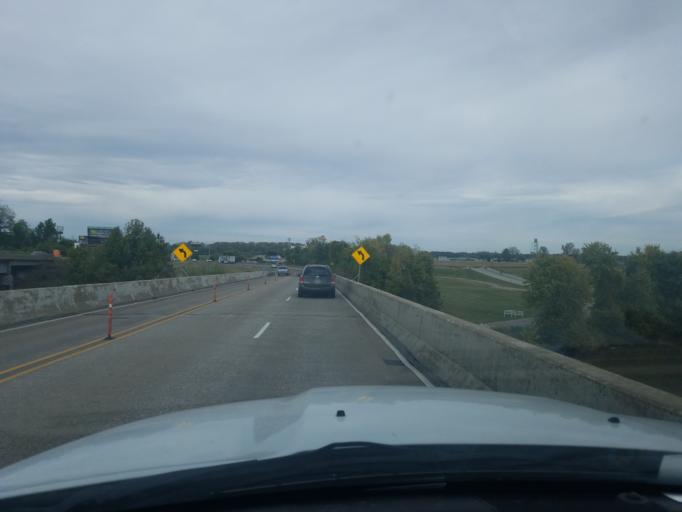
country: US
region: Indiana
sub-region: Vanderburgh County
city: Evansville
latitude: 37.9109
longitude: -87.5480
